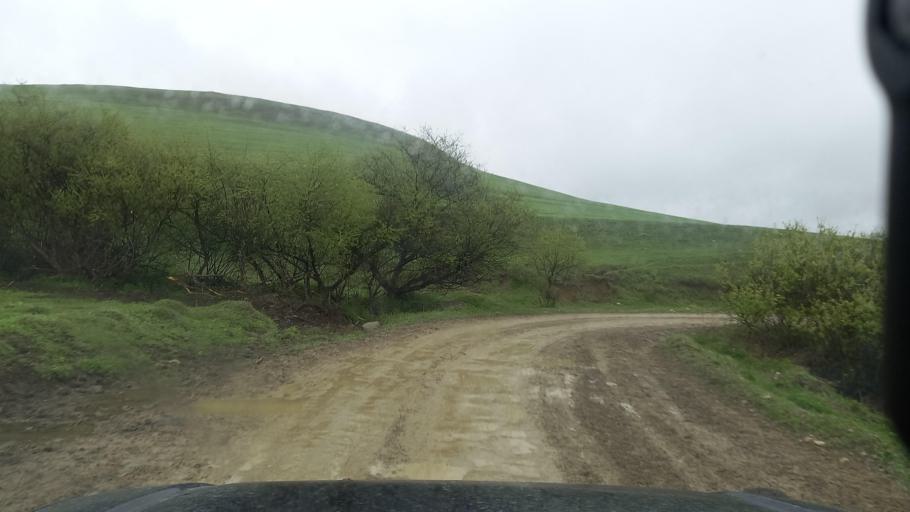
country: RU
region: Kabardino-Balkariya
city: Gundelen
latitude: 43.5947
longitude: 43.1237
